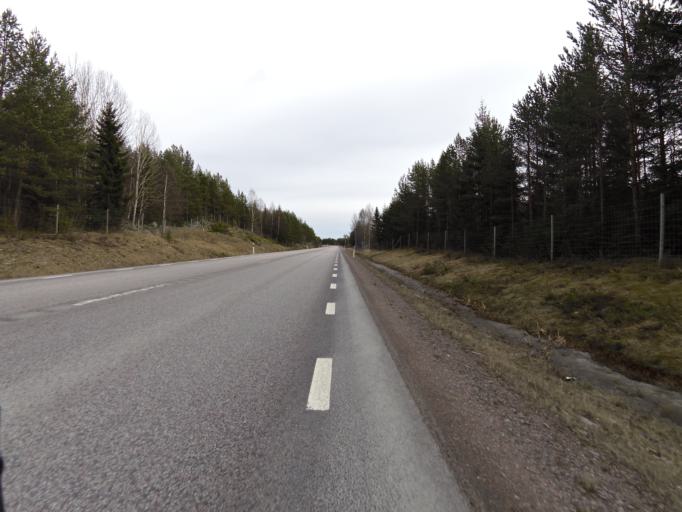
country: SE
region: Gaevleborg
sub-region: Hofors Kommun
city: Hofors
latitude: 60.5415
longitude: 16.1768
